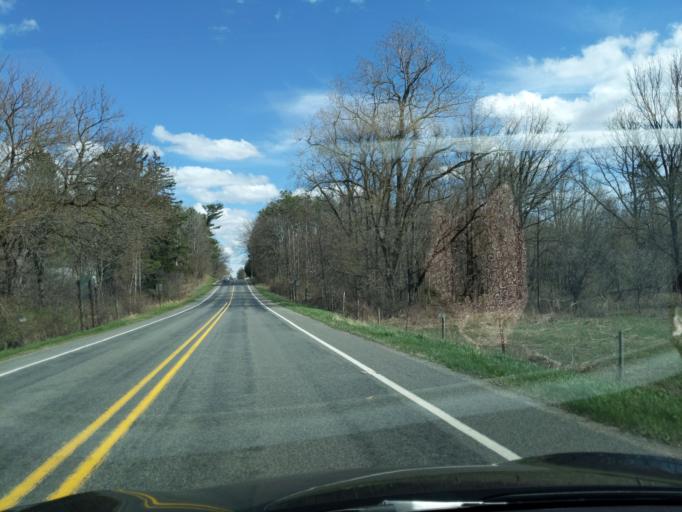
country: US
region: Michigan
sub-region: Ingham County
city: Mason
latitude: 42.5520
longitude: -84.3877
